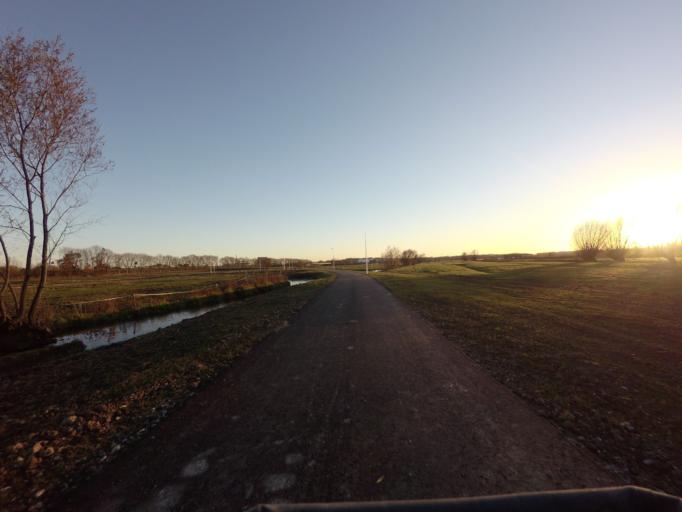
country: NL
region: Utrecht
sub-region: Gemeente Nieuwegein
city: Nieuwegein
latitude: 52.0802
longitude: 5.0693
